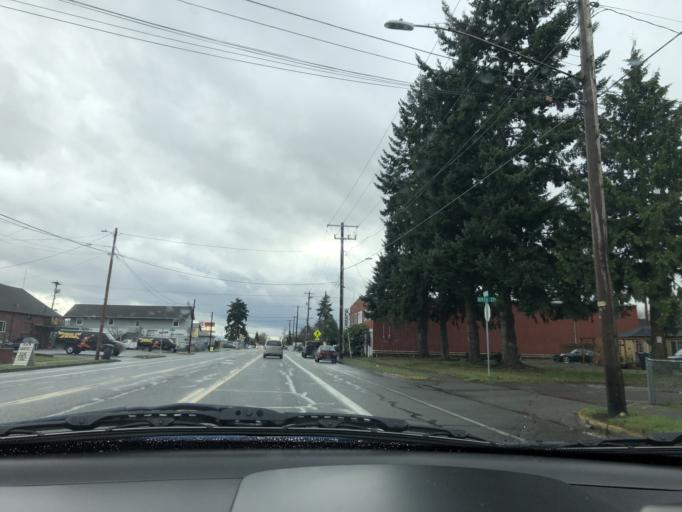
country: US
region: Washington
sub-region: Snohomish County
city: Marysville
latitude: 48.0567
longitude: -122.1805
